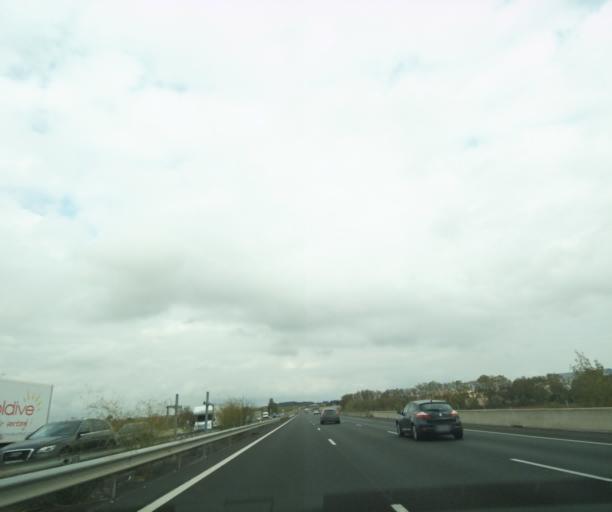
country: FR
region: Languedoc-Roussillon
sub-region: Departement de l'Herault
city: Florensac
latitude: 43.3886
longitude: 3.4579
